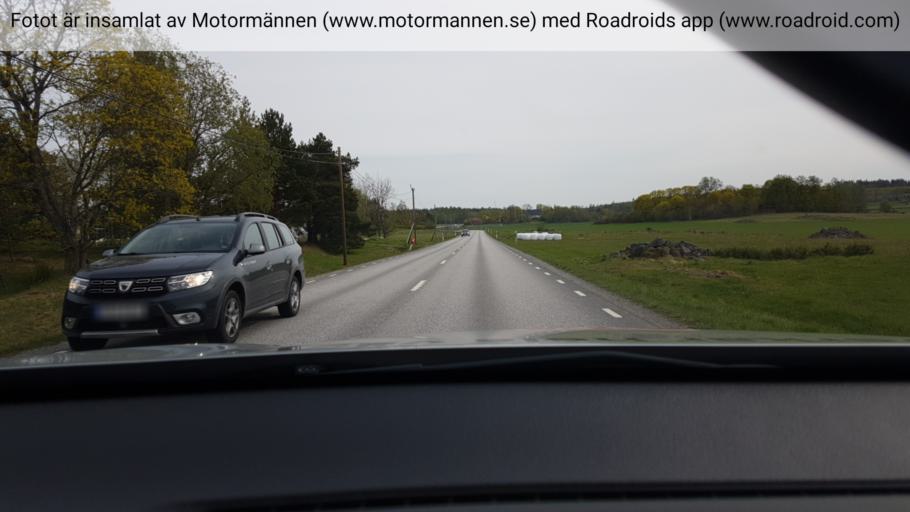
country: SE
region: Stockholm
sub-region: Vallentuna Kommun
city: Vallentuna
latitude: 59.6760
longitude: 18.0437
